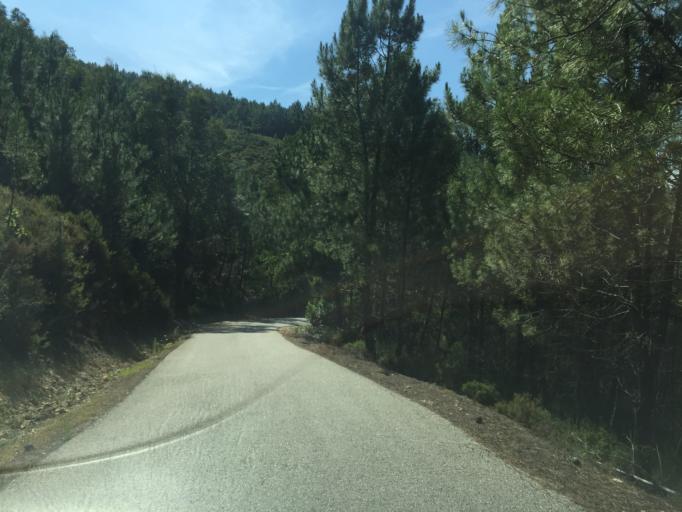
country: PT
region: Castelo Branco
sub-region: Oleiros
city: Oleiros
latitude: 39.9808
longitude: -7.8474
